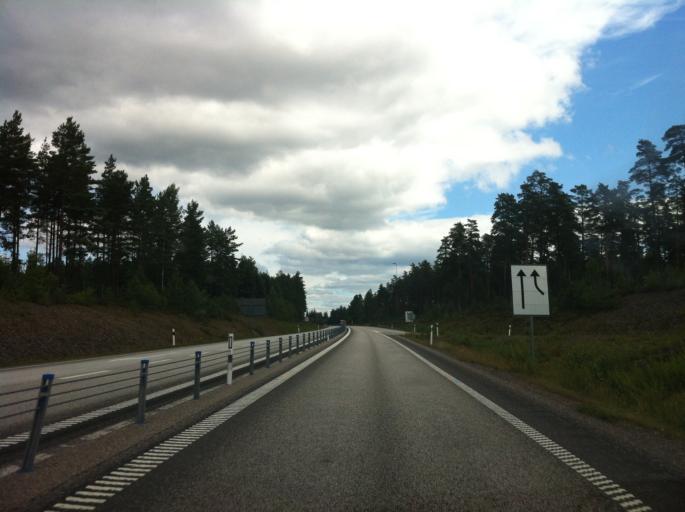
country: SE
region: Joenkoeping
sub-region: Gislaveds Kommun
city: Gislaved
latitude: 57.3244
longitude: 13.5443
